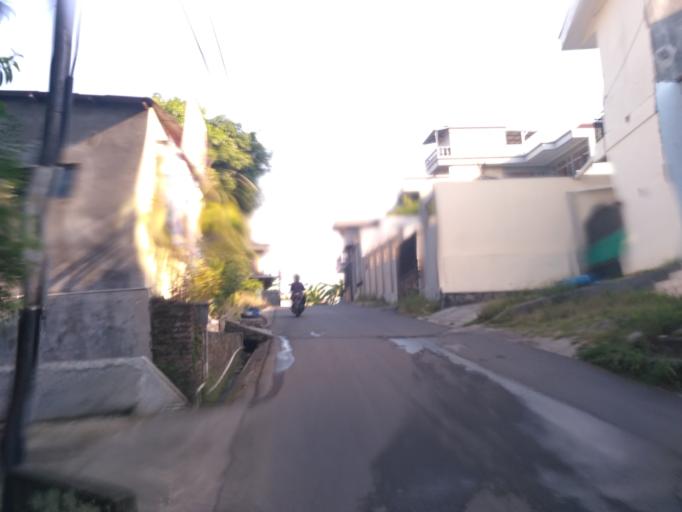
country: ID
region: Central Java
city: Mranggen
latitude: -7.0168
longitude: 110.4663
